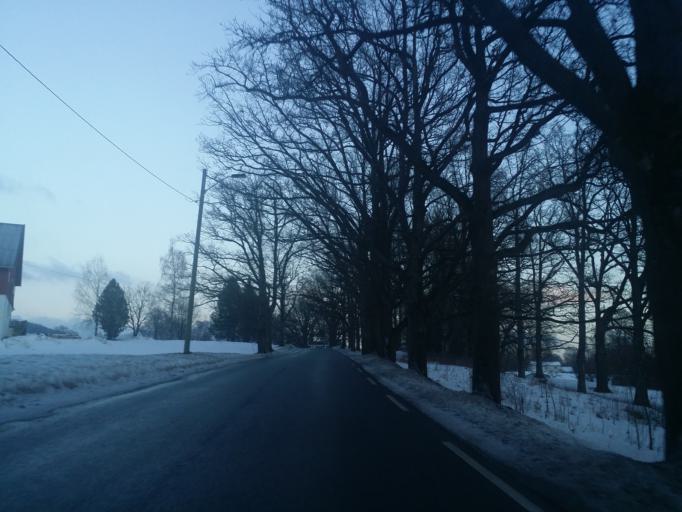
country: NO
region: Akershus
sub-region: Baerum
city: Skui
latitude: 59.9127
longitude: 10.4809
